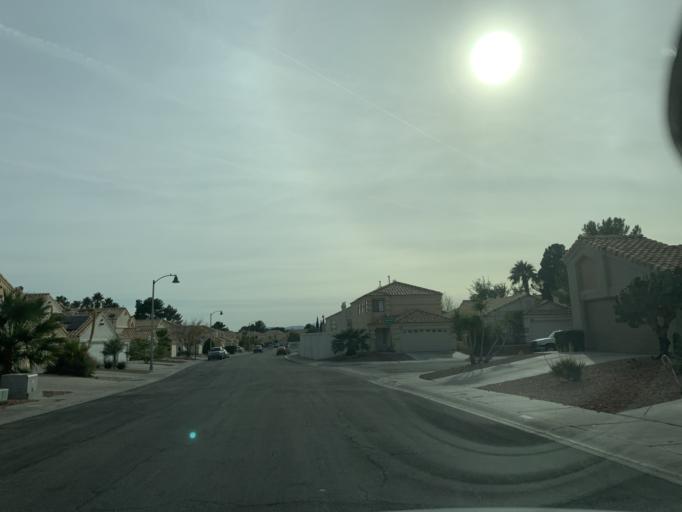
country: US
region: Nevada
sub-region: Clark County
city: Summerlin South
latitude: 36.1365
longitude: -115.3024
